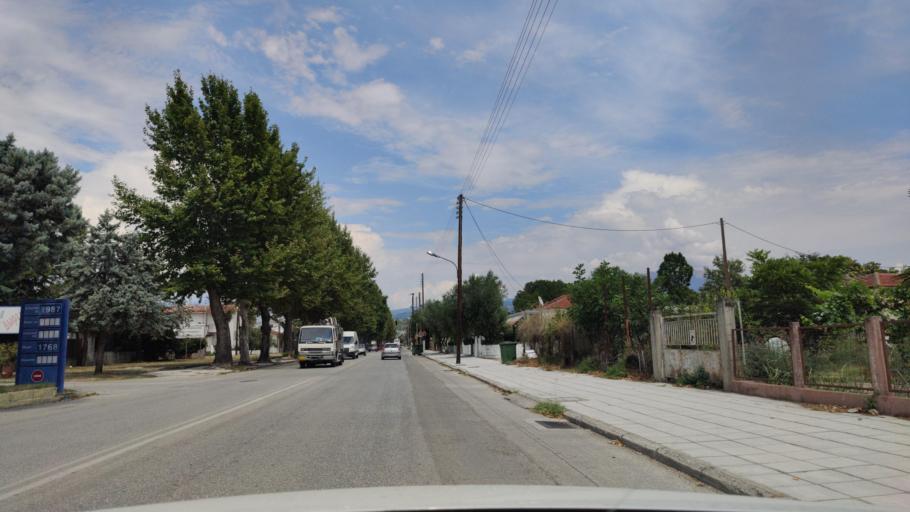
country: GR
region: Central Macedonia
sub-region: Nomos Serron
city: Serres
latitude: 41.0771
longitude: 23.5388
